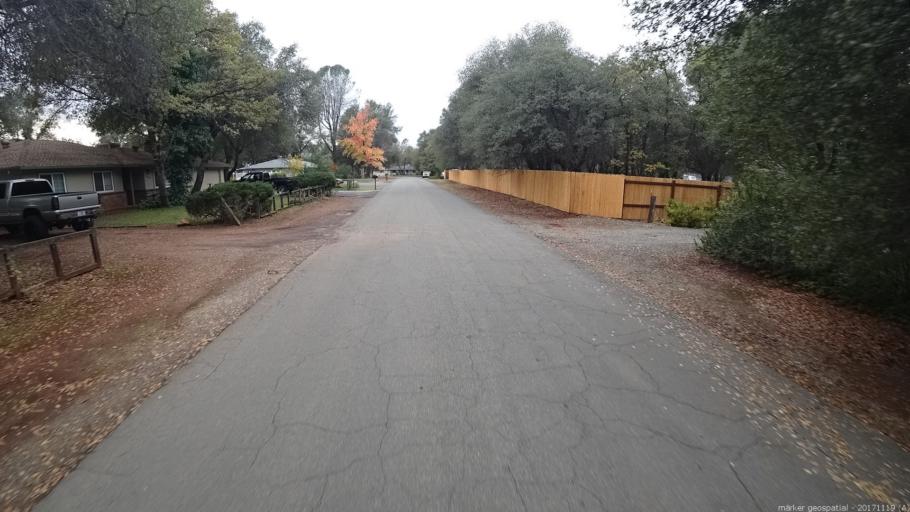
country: US
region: California
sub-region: Shasta County
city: Redding
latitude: 40.4882
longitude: -122.4198
